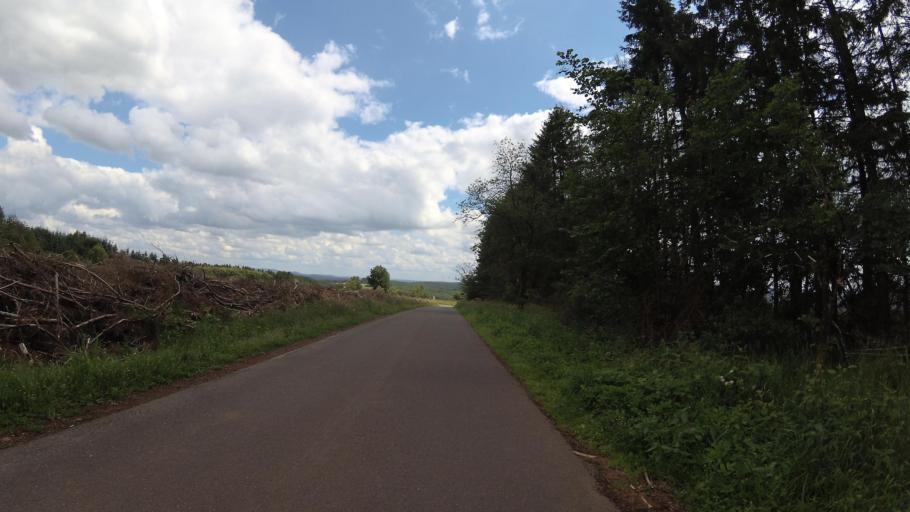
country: DE
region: Rheinland-Pfalz
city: Neuhutten
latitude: 49.5720
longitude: 7.0115
